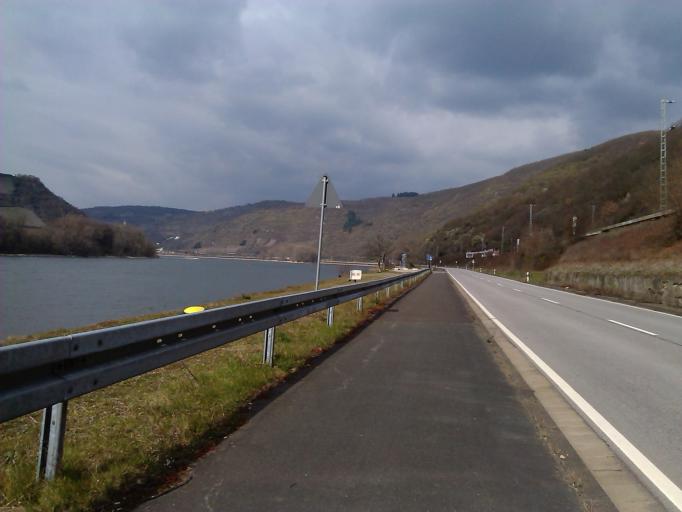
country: DE
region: Rheinland-Pfalz
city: Bacharach
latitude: 50.0614
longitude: 7.7756
